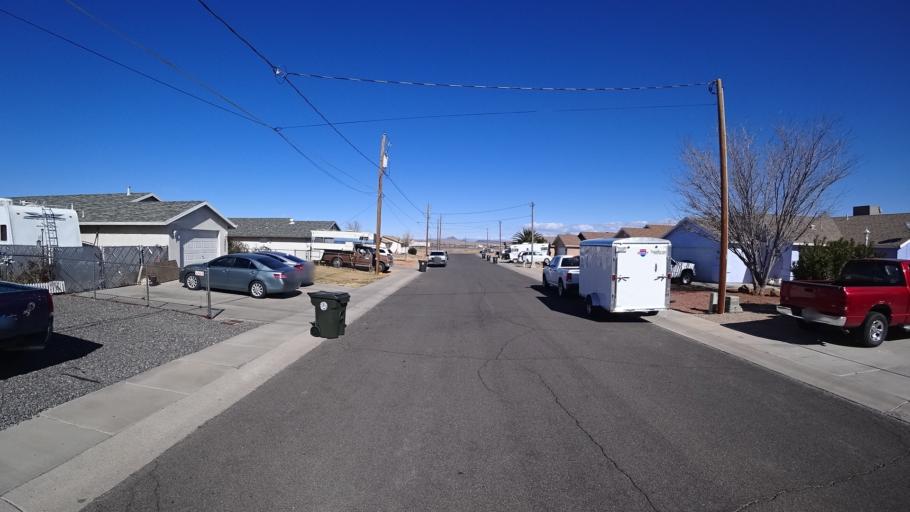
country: US
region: Arizona
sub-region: Mohave County
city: New Kingman-Butler
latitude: 35.2200
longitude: -114.0026
